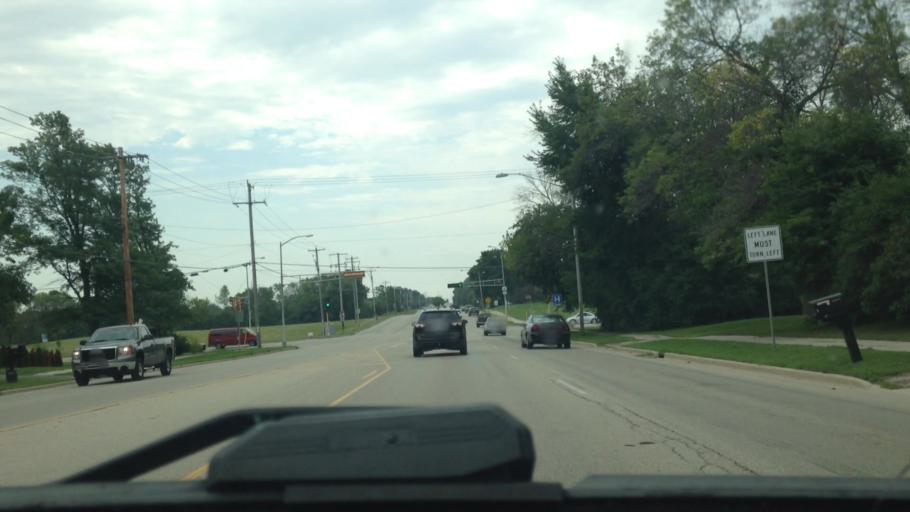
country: US
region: Wisconsin
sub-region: Waukesha County
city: Menomonee Falls
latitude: 43.1493
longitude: -88.1045
